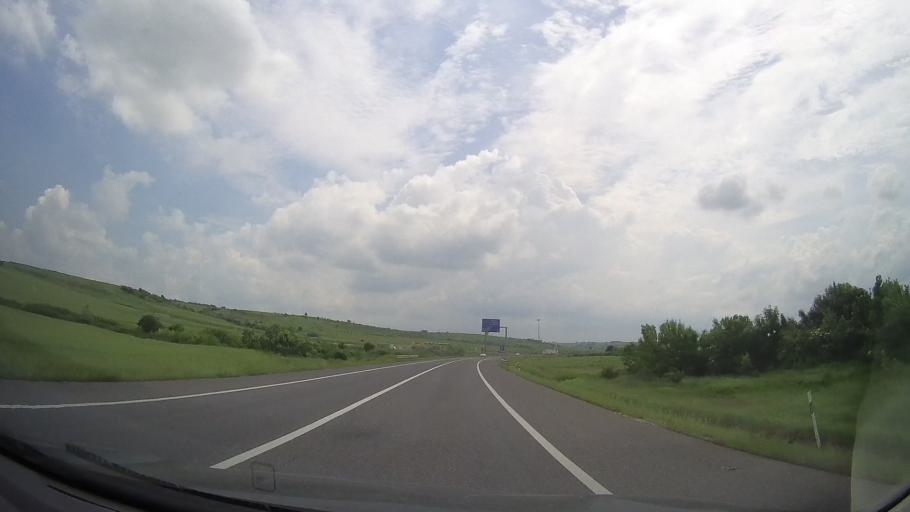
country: RO
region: Timis
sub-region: Municipiul Lugoj
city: Lugoj
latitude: 45.7217
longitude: 21.8928
